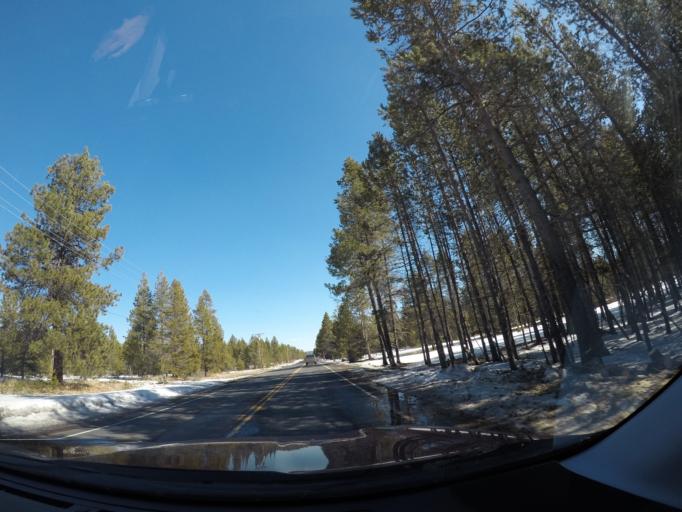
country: US
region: Oregon
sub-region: Deschutes County
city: Sunriver
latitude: 43.8629
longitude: -121.4700
